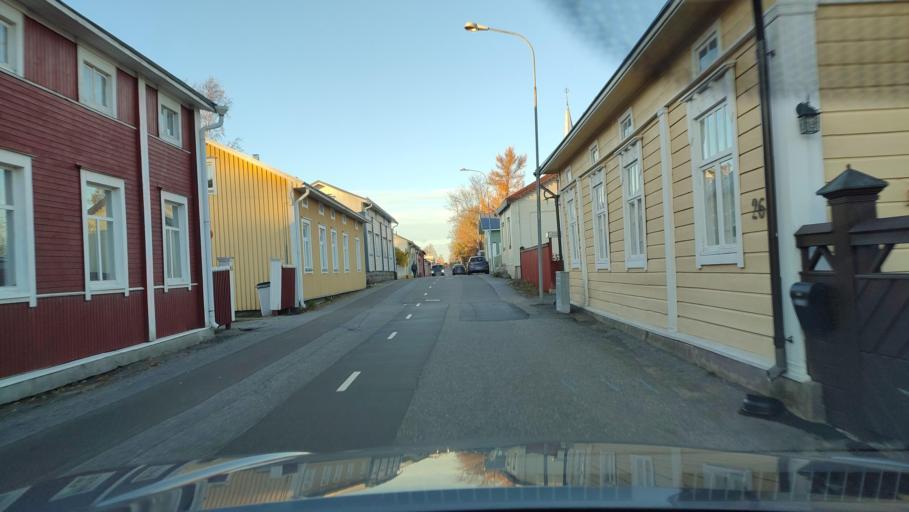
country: FI
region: Ostrobothnia
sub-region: Sydosterbotten
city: Kristinestad
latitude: 62.2710
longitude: 21.3752
